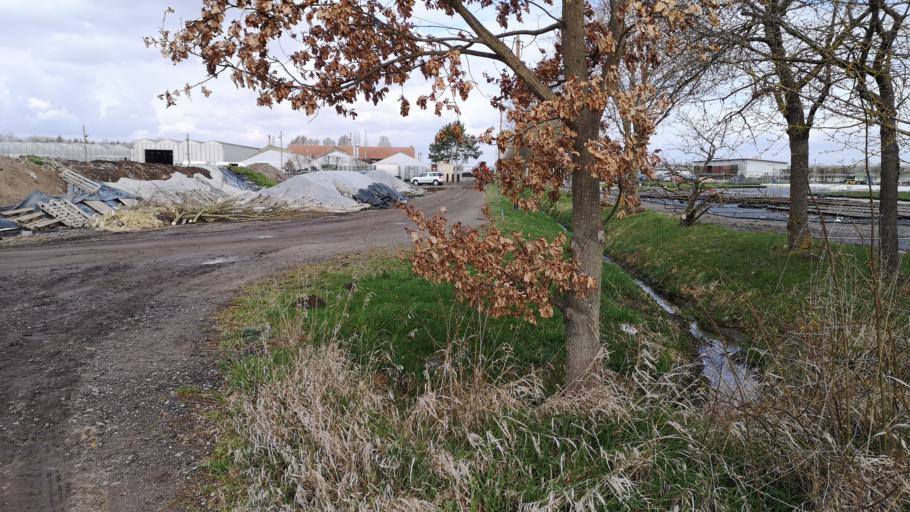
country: DE
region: Bavaria
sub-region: Regierungsbezirk Unterfranken
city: Gochsheim
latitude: 49.9956
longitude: 10.2804
